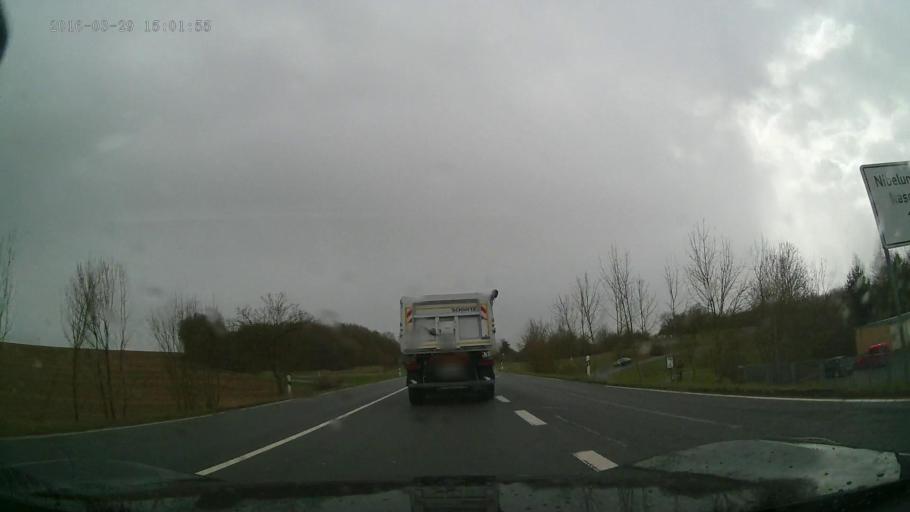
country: DE
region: Baden-Wuerttemberg
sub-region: Karlsruhe Region
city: Walldurn
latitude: 49.5654
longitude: 9.3626
